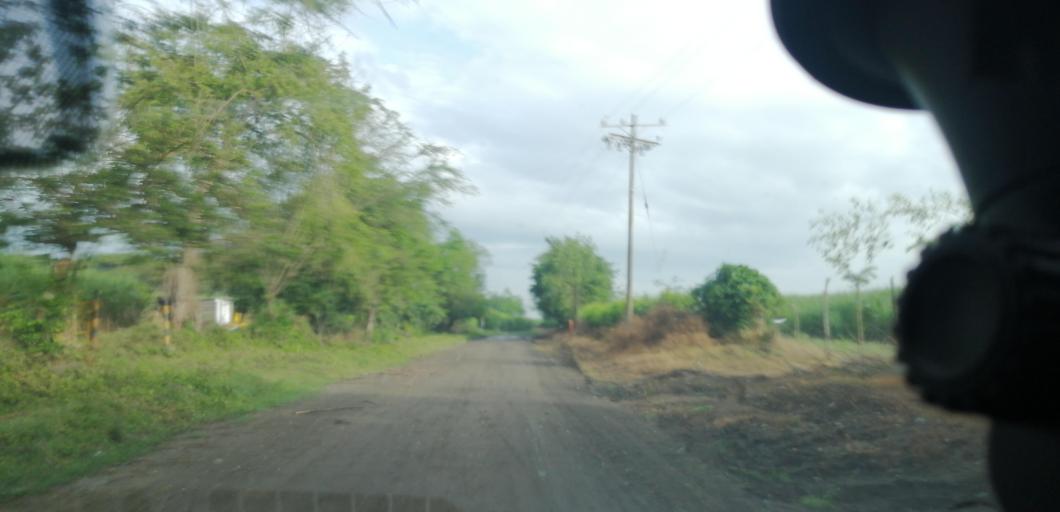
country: CO
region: Valle del Cauca
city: Palmira
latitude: 3.5510
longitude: -76.3632
